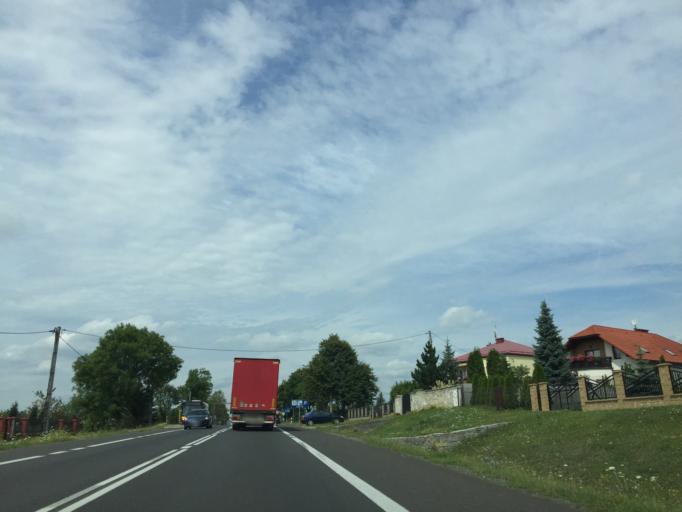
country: PL
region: Lesser Poland Voivodeship
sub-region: Powiat krakowski
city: Przeginia
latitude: 50.2545
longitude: 19.6463
